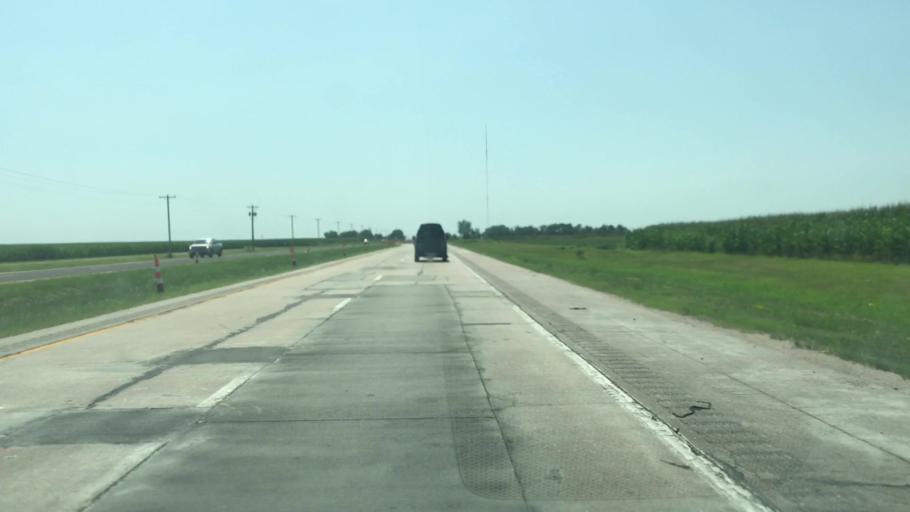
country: US
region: Nebraska
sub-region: Adams County
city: Hastings
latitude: 40.6651
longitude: -98.3824
